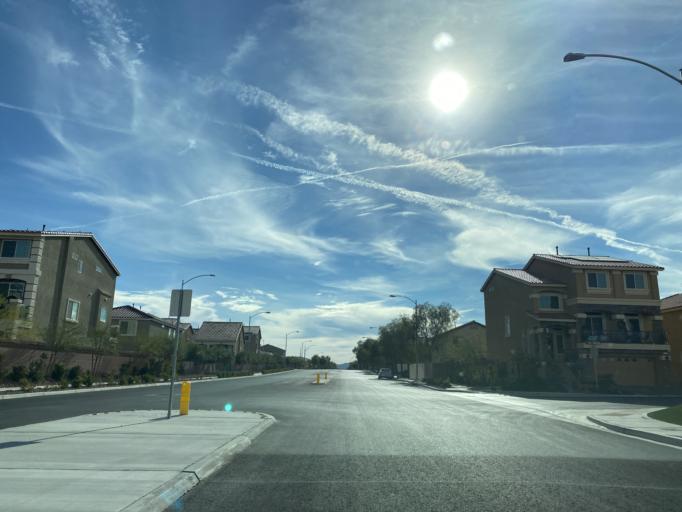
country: US
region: Nevada
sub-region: Clark County
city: Enterprise
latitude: 36.0586
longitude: -115.2339
